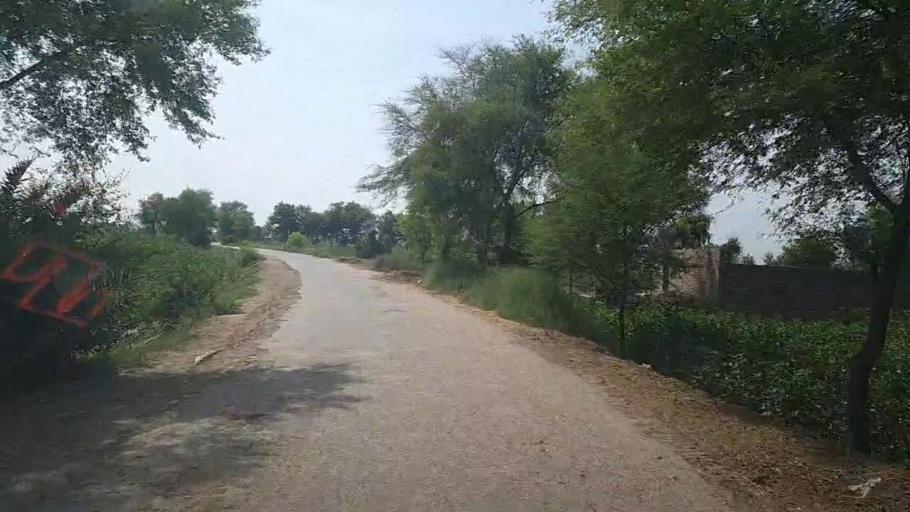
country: PK
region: Sindh
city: Ubauro
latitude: 28.1343
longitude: 69.8333
